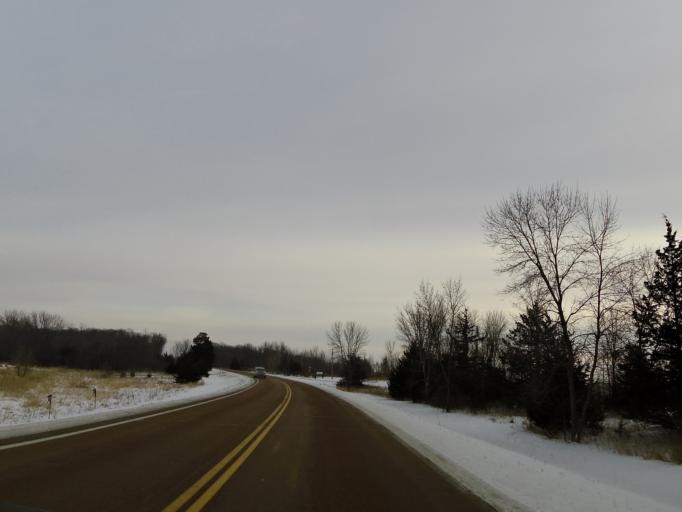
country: US
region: Minnesota
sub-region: Carver County
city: Victoria
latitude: 44.8751
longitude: -93.6914
